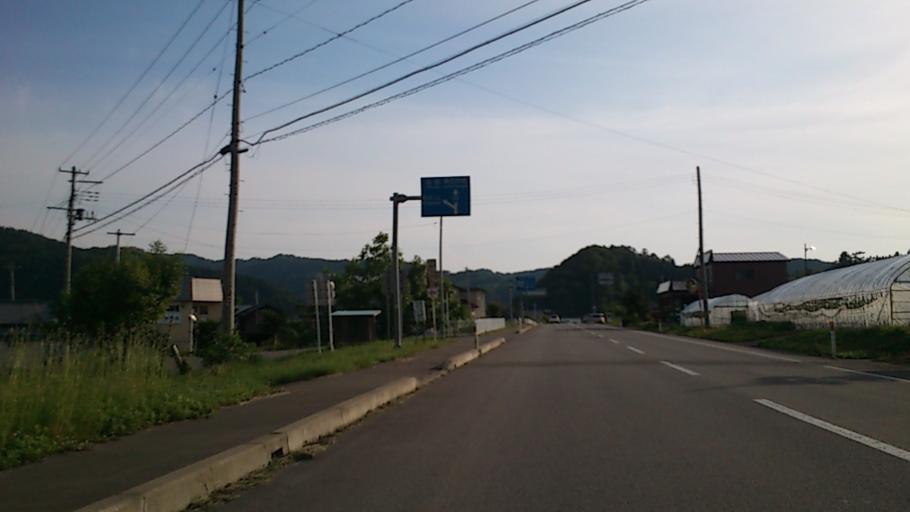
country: JP
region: Aomori
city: Kuroishi
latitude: 40.6125
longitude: 140.6809
